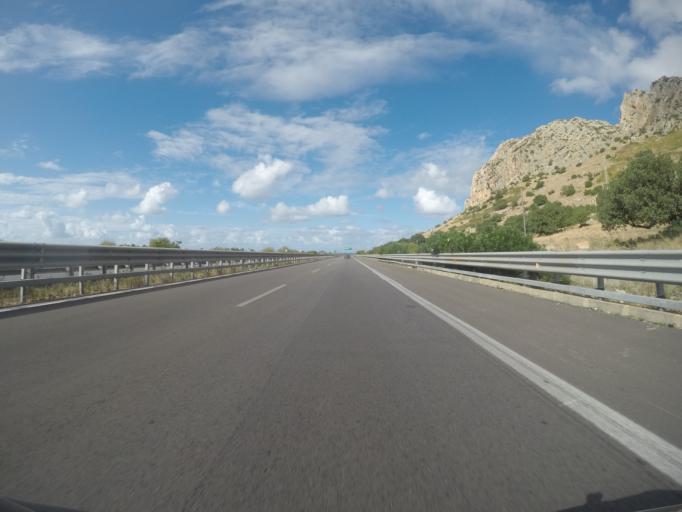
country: IT
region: Sicily
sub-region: Palermo
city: Cinisi
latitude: 38.1672
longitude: 13.1124
